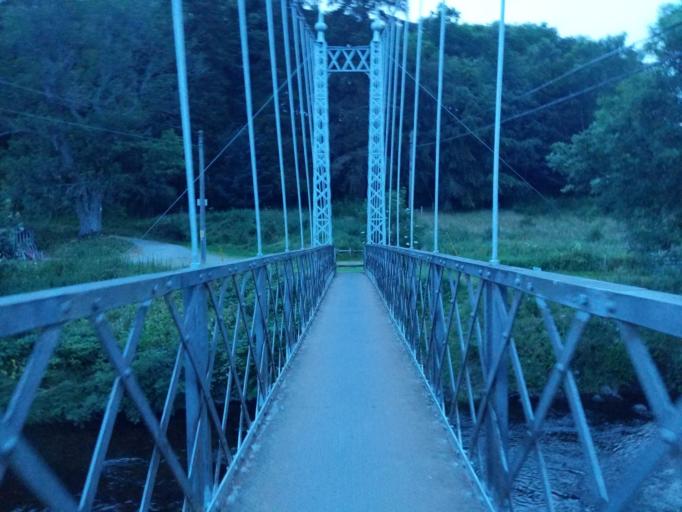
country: GB
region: Scotland
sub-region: Moray
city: Rothes
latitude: 57.4705
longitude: -3.2319
